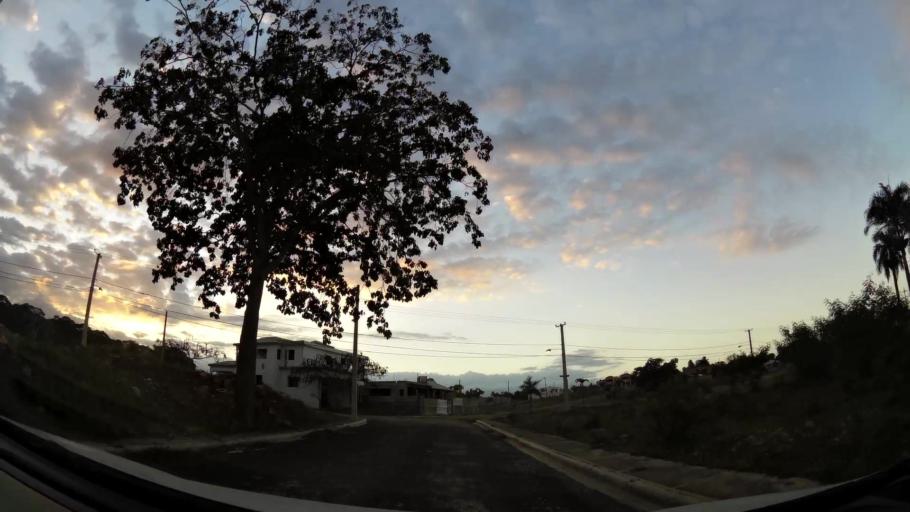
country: DO
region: Nacional
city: La Agustina
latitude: 18.5652
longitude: -69.9367
